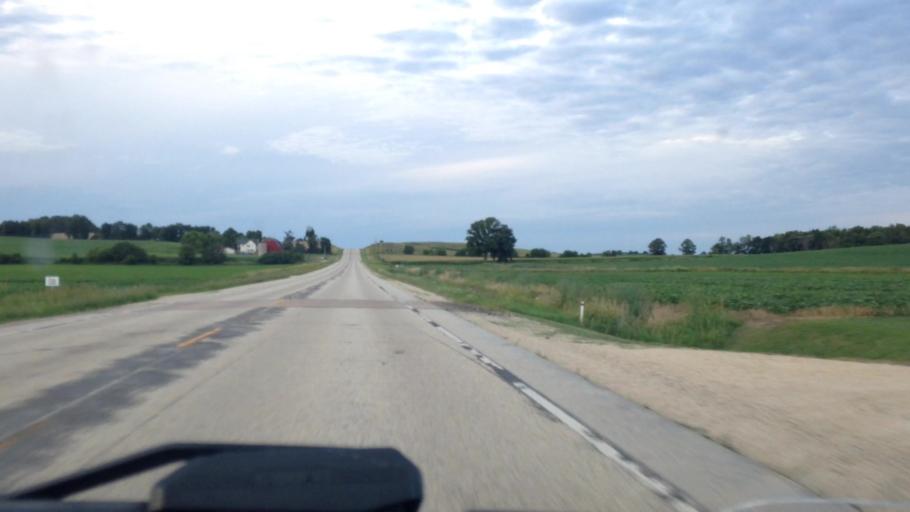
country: US
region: Wisconsin
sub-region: Dodge County
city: Theresa
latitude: 43.4727
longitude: -88.4501
